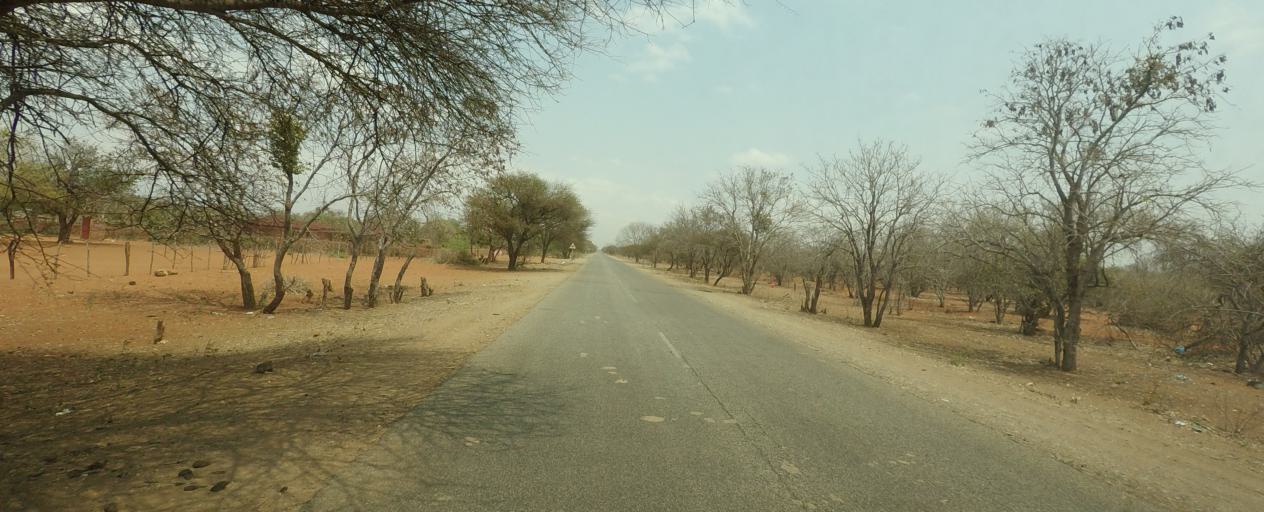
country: ZA
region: Limpopo
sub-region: Vhembe District Municipality
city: Mutale
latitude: -22.4221
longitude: 30.9052
